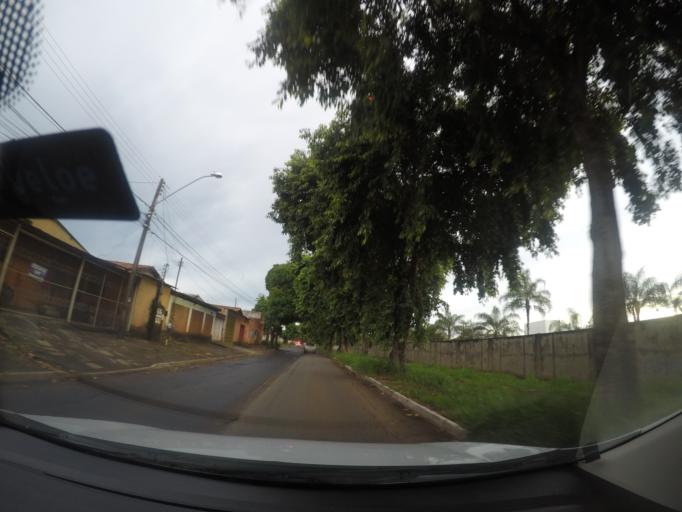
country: BR
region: Goias
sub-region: Goiania
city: Goiania
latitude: -16.7255
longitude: -49.3100
